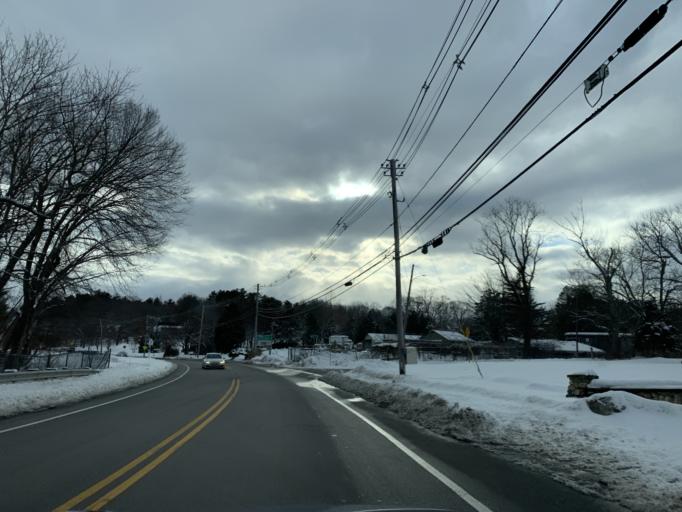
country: US
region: Massachusetts
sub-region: Norfolk County
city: Franklin
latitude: 42.0557
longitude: -71.4335
